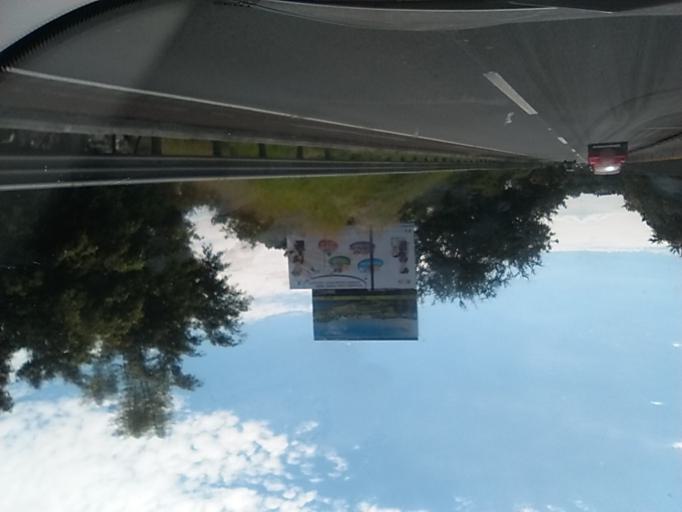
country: MX
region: Morelos
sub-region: Emiliano Zapata
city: Tres de Mayo
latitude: 18.8752
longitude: -99.2272
